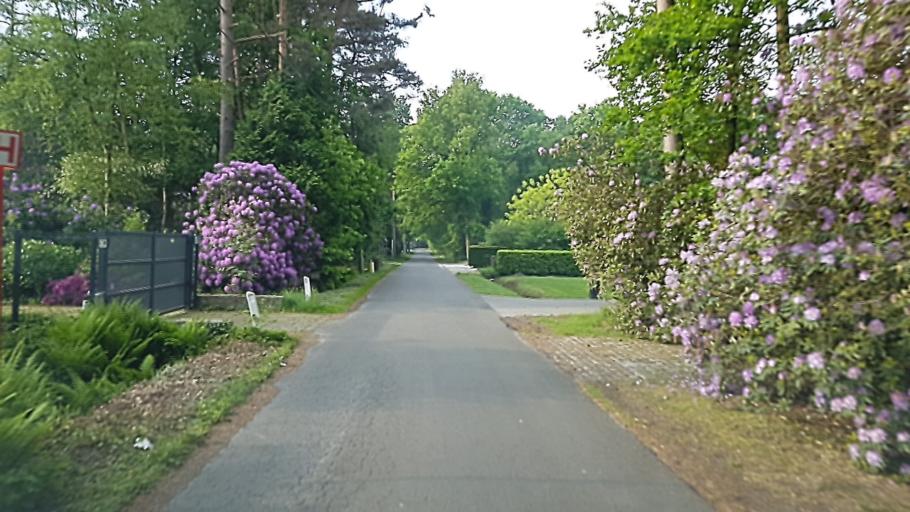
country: BE
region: Flanders
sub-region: Provincie Antwerpen
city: Zoersel
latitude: 51.2710
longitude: 4.6651
